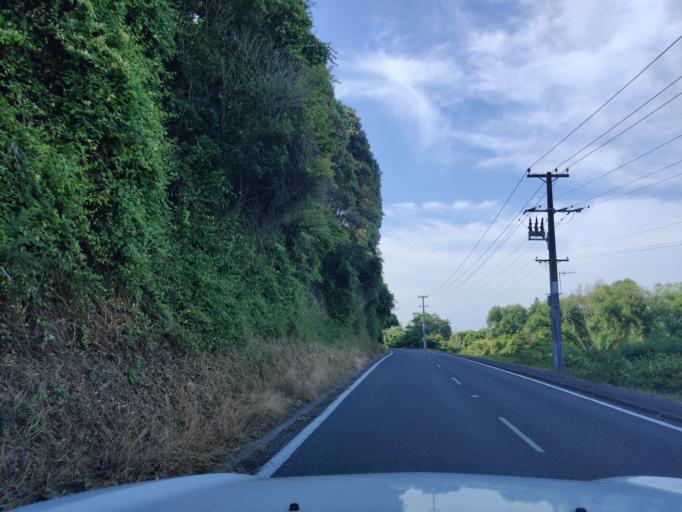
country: NZ
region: Waikato
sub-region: Waikato District
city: Ngaruawahia
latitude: -37.5767
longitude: 175.1532
